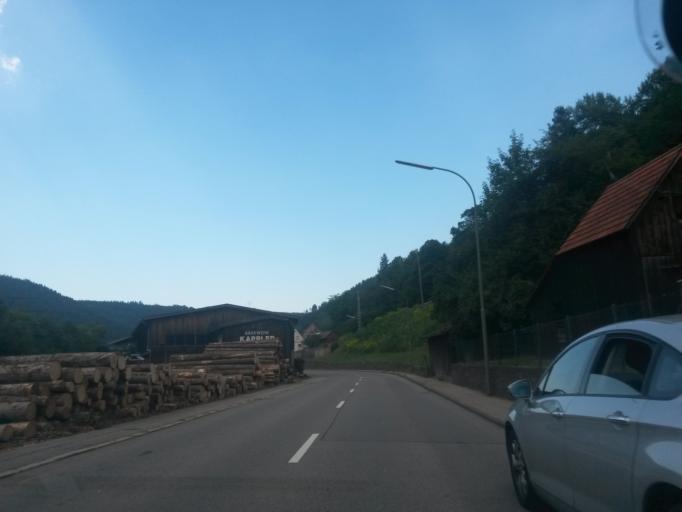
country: DE
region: Baden-Wuerttemberg
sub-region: Karlsruhe Region
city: Hofen an der Enz
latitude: 48.7673
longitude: 8.5868
